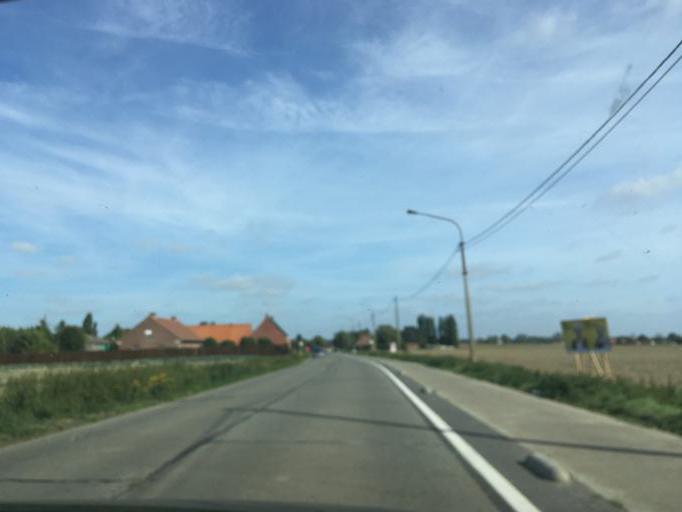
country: BE
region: Flanders
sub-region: Provincie West-Vlaanderen
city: Moorslede
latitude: 50.9214
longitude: 3.0850
